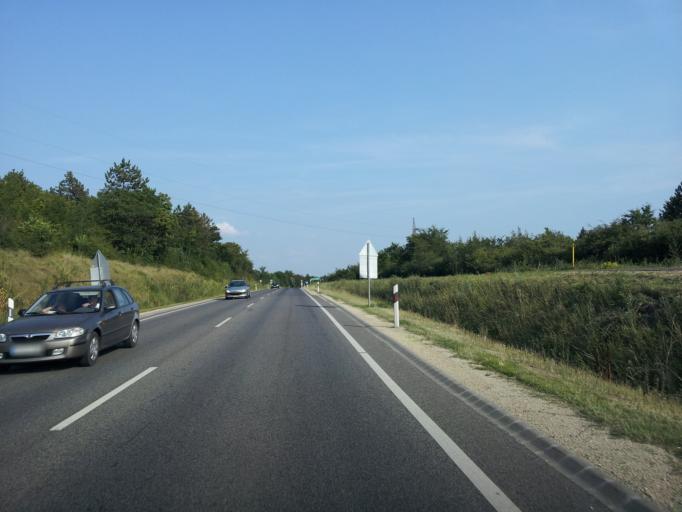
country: HU
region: Veszprem
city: Liter
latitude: 47.0955
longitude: 18.0214
